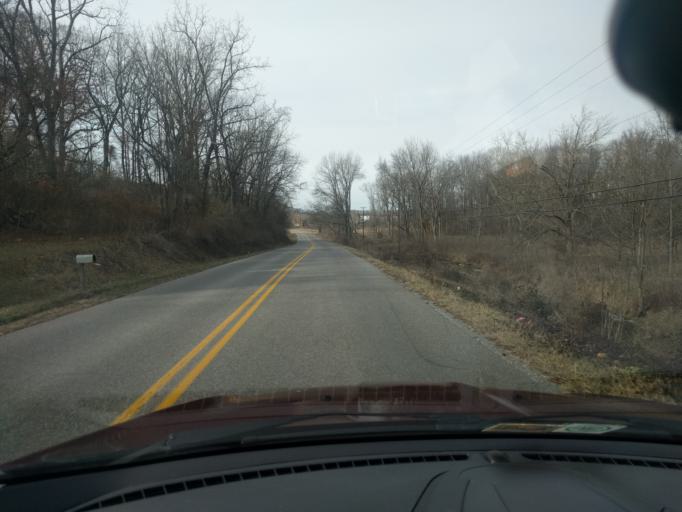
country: US
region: Virginia
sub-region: Augusta County
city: Stuarts Draft
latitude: 37.9276
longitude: -79.2074
